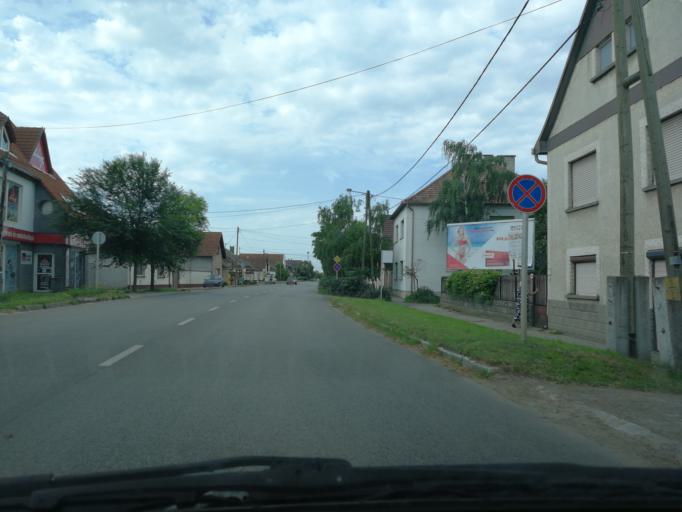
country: HU
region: Bacs-Kiskun
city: Baja
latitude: 46.2071
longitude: 18.9610
